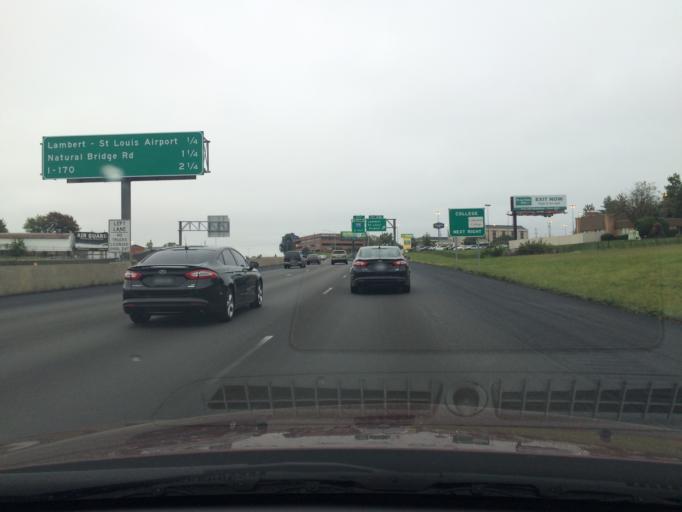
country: US
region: Missouri
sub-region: Saint Louis County
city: Saint Ann
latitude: 38.7413
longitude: -90.3753
